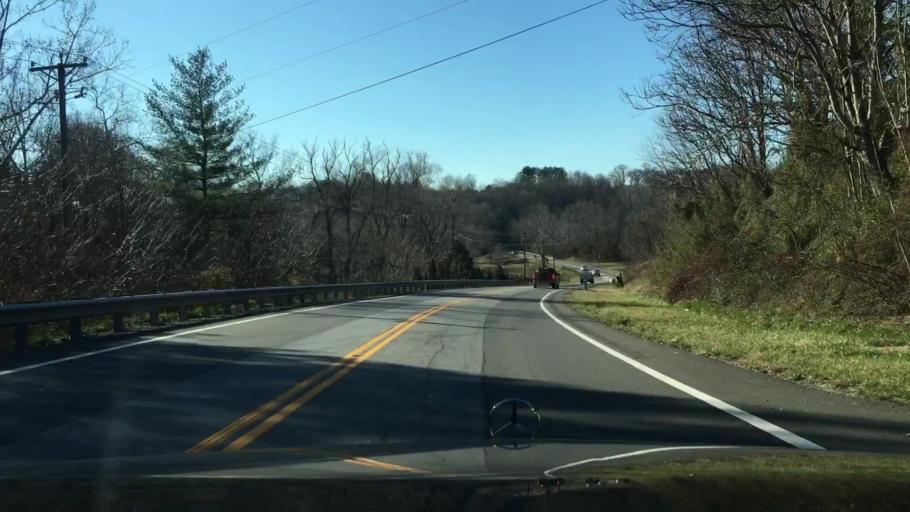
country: US
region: Virginia
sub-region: Botetourt County
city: Blue Ridge
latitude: 37.2712
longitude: -79.7704
